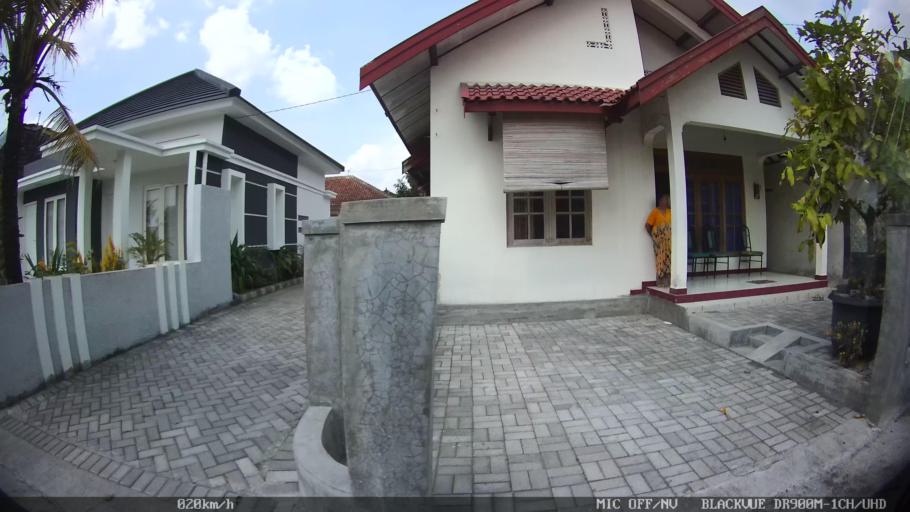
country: ID
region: Daerah Istimewa Yogyakarta
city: Depok
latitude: -7.8013
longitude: 110.4076
